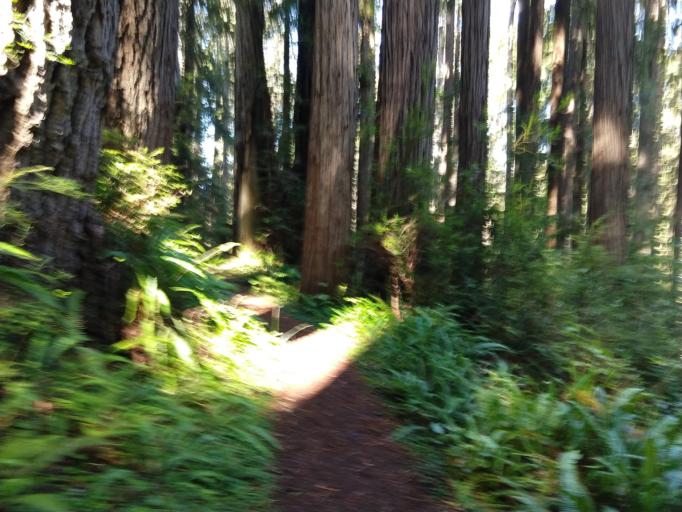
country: US
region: California
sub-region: Humboldt County
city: Westhaven-Moonstone
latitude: 41.3888
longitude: -124.0500
